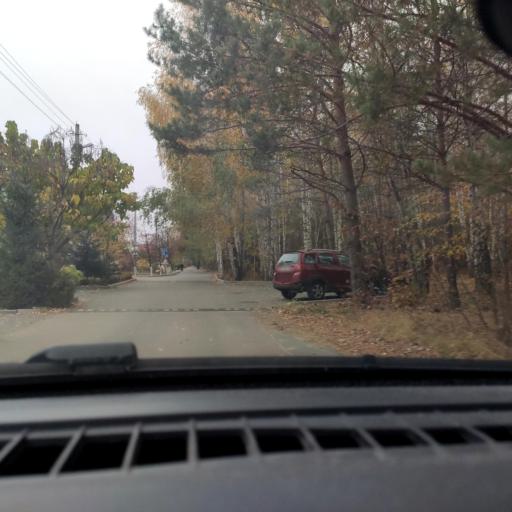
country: RU
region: Voronezj
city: Podgornoye
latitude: 51.7616
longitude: 39.1872
